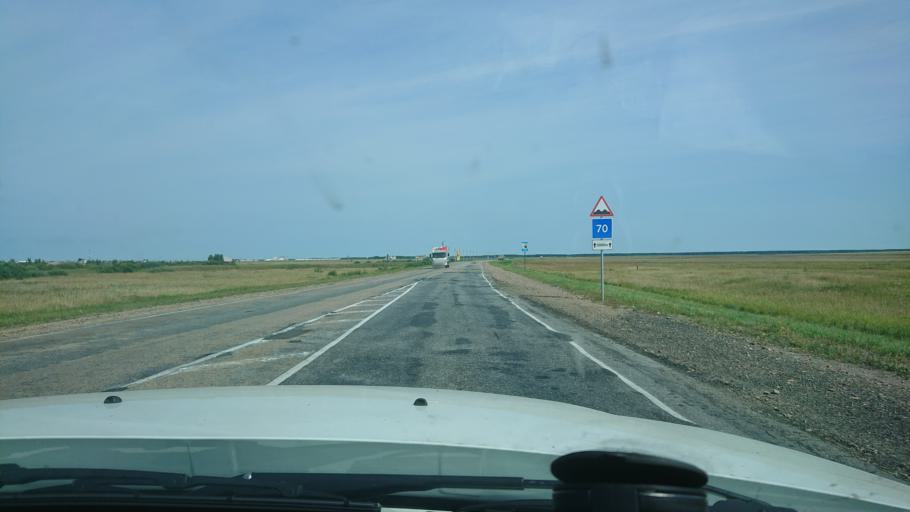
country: RU
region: Kurgan
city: Petukhovo
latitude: 55.5334
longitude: 67.8886
